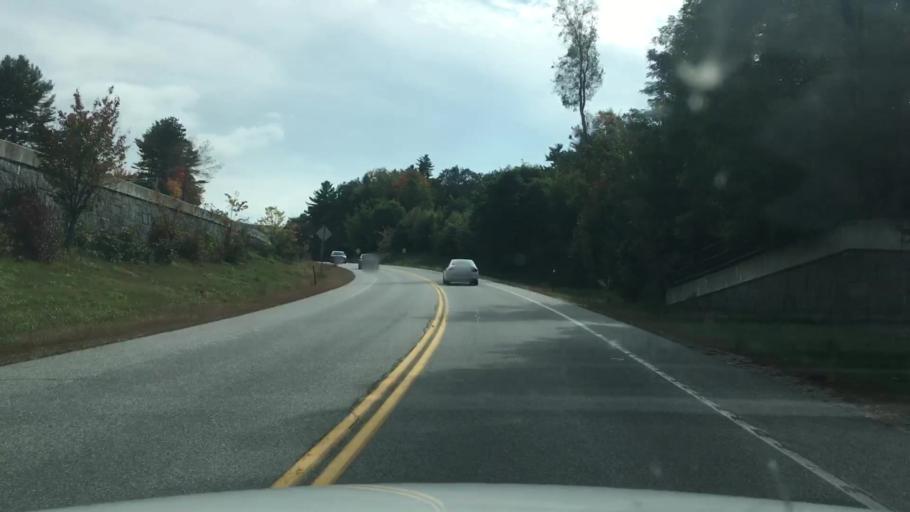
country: US
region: New Hampshire
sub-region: Carroll County
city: North Conway
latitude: 44.0443
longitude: -71.1219
